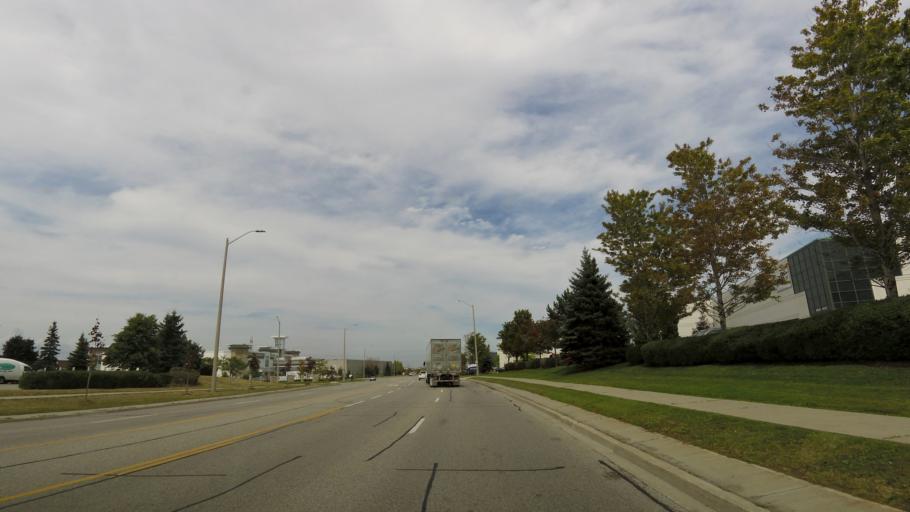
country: CA
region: Ontario
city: Mississauga
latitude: 43.6438
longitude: -79.6868
